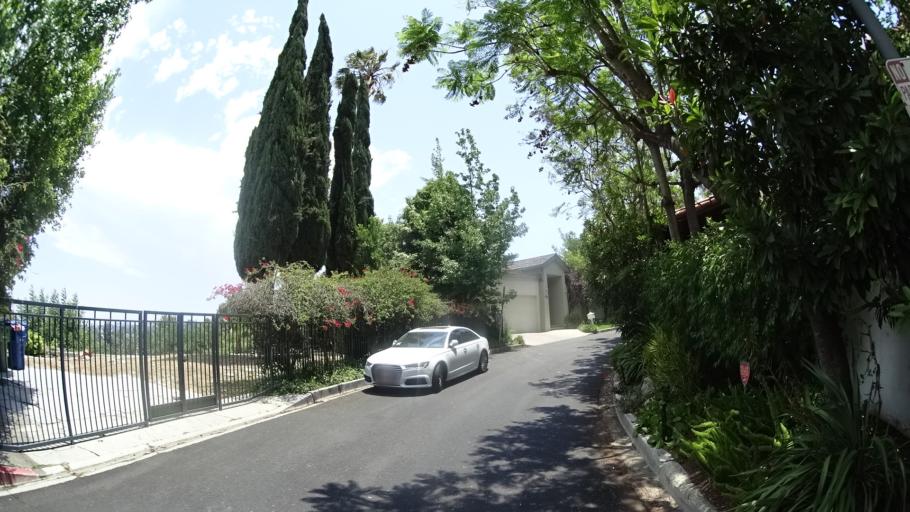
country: US
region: California
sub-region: Los Angeles County
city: Sherman Oaks
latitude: 34.1420
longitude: -118.4348
